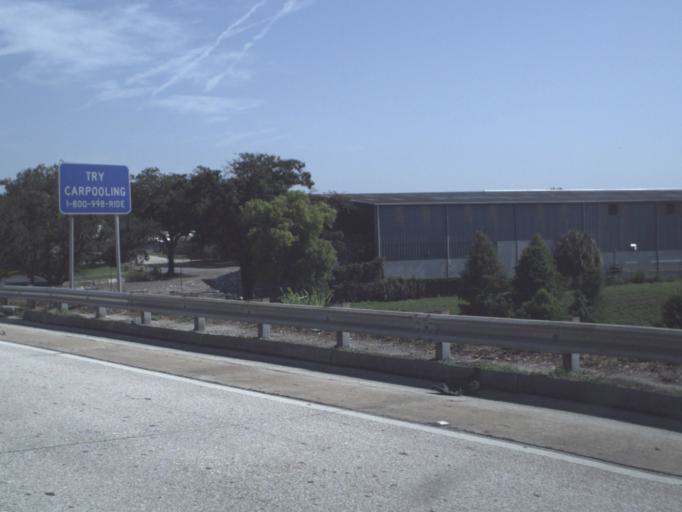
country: US
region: Florida
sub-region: Pinellas County
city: Saint Petersburg
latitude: 27.7821
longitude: -82.6609
